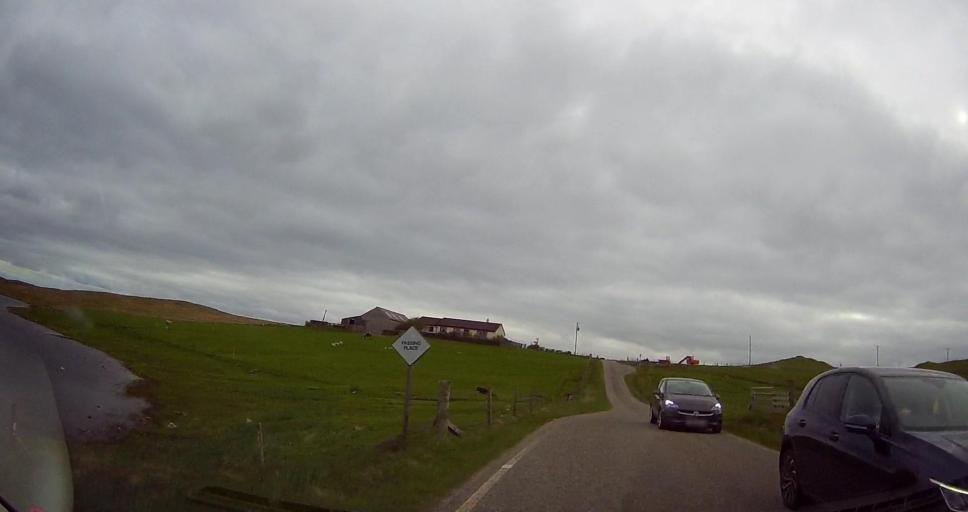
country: GB
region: Scotland
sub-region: Shetland Islands
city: Shetland
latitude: 60.4997
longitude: -1.0763
